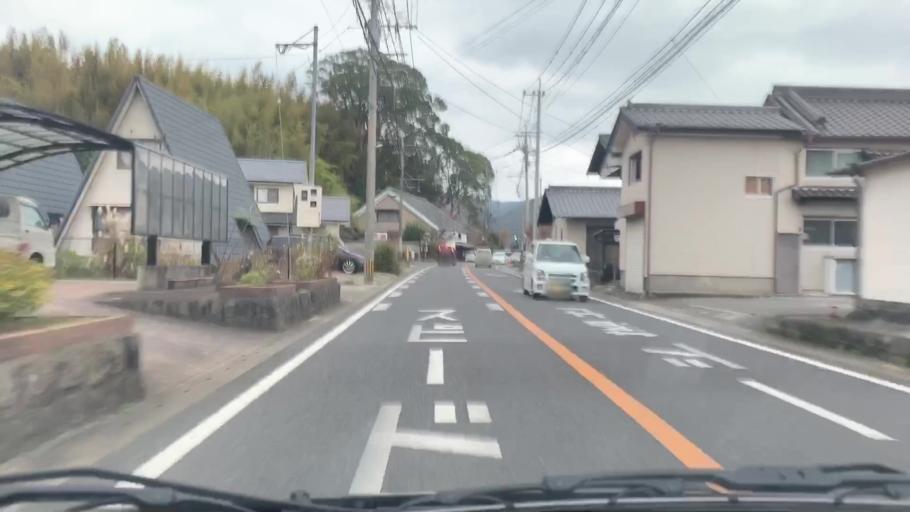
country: JP
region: Saga Prefecture
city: Kashima
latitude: 33.1351
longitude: 130.0627
